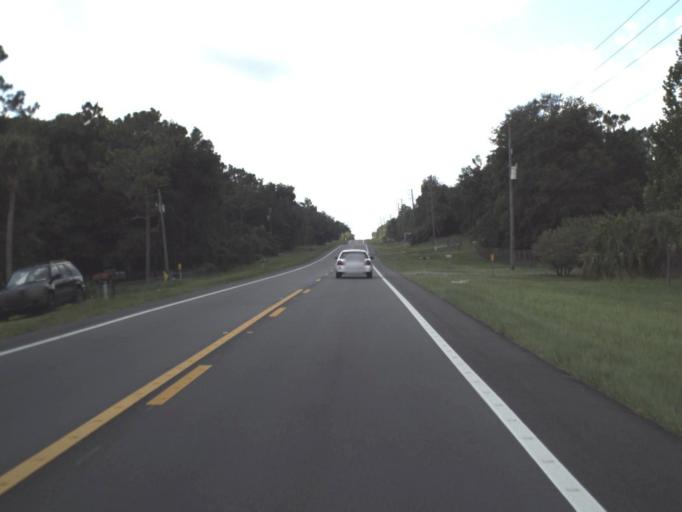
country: US
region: Florida
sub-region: Citrus County
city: Floral City
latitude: 28.6977
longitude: -82.3162
